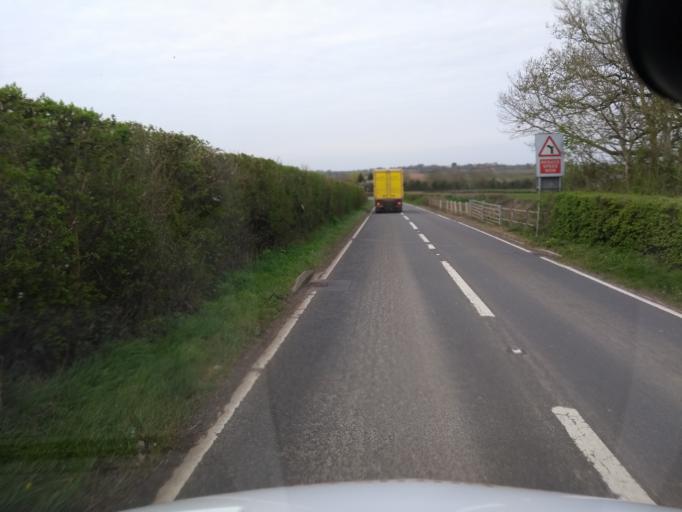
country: GB
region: England
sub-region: Somerset
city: Creech Saint Michael
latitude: 51.0055
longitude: -2.9554
